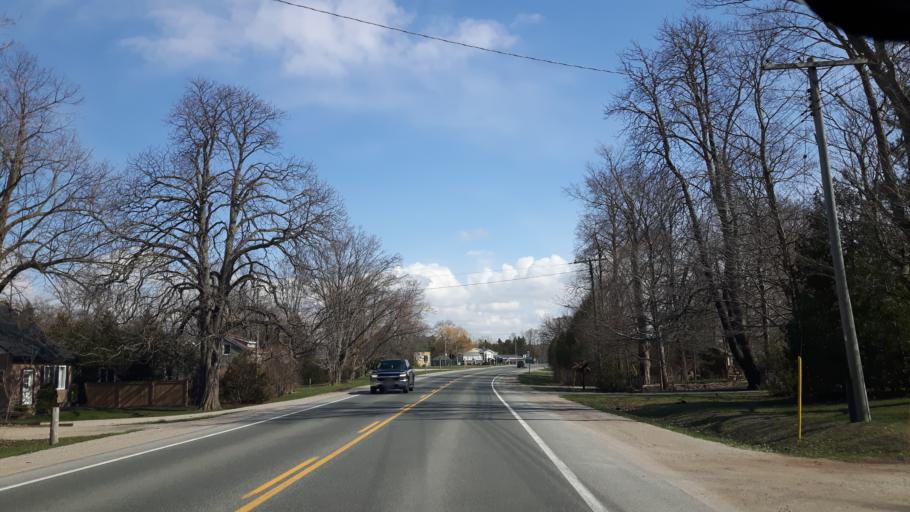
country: CA
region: Ontario
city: Bluewater
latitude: 43.5586
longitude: -81.6929
